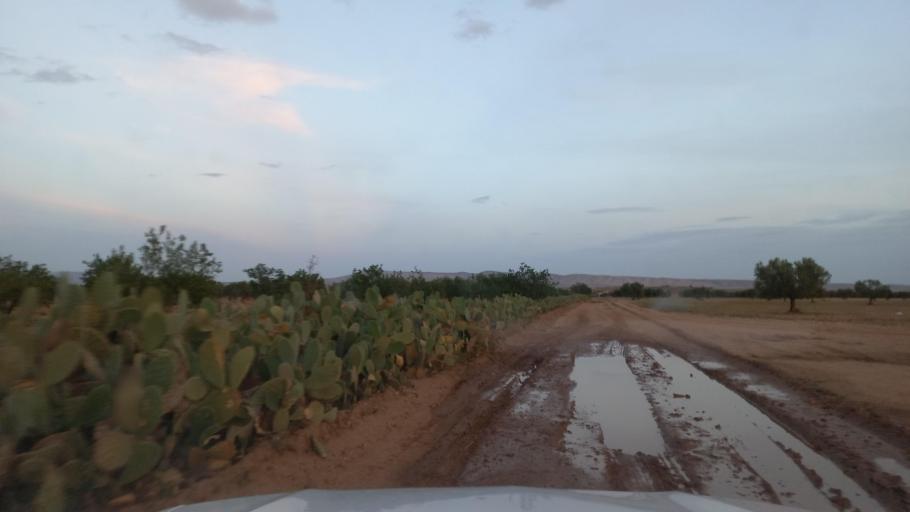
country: TN
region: Al Qasrayn
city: Sbiba
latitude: 35.3482
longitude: 9.0504
